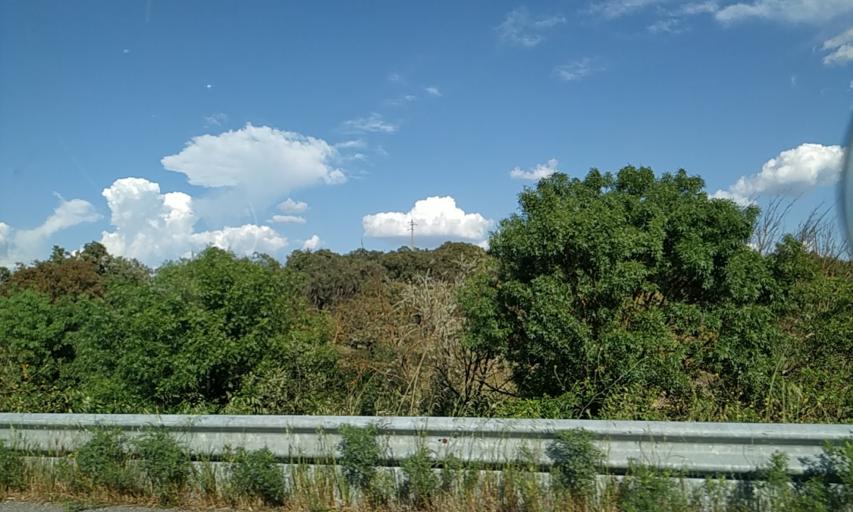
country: PT
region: Evora
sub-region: Estremoz
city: Estremoz
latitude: 38.9889
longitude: -7.4758
